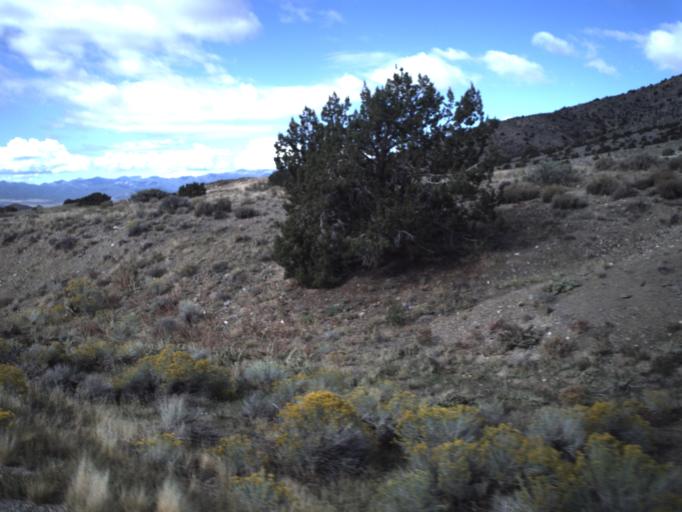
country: US
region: Utah
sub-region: Beaver County
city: Milford
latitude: 38.4414
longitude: -113.2677
